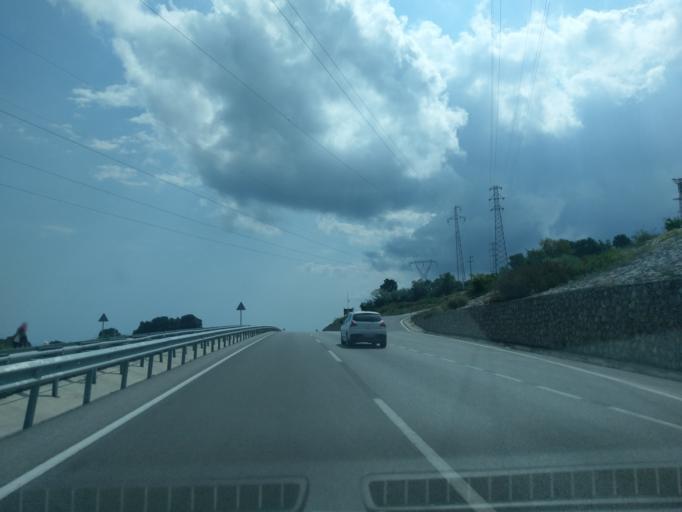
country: TR
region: Sinop
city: Kabali
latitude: 41.8532
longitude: 35.1175
